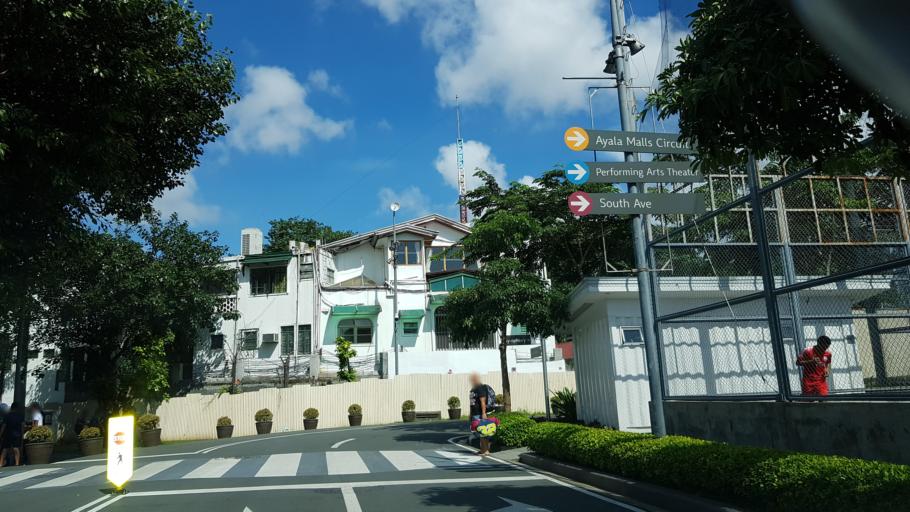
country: PH
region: Metro Manila
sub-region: Mandaluyong
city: Mandaluyong City
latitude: 14.5762
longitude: 121.0209
